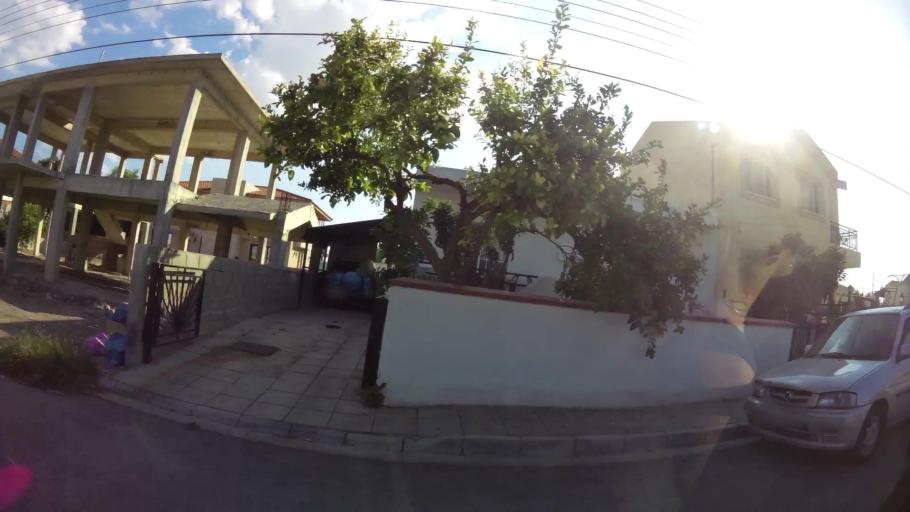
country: CY
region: Larnaka
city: Aradippou
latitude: 34.9469
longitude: 33.6006
